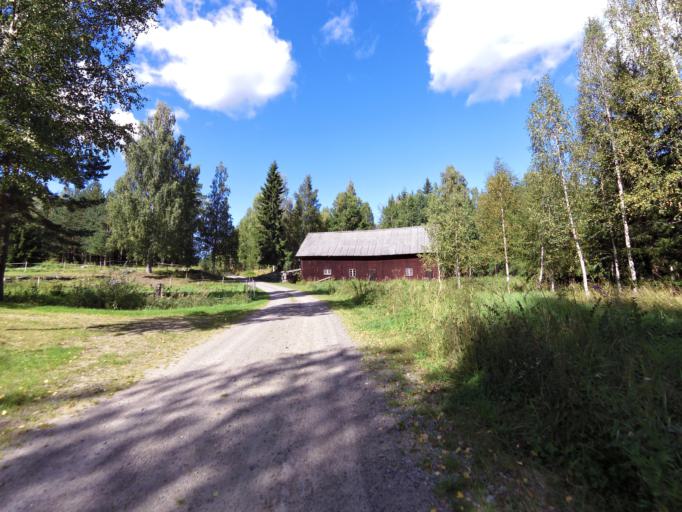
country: SE
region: Gaevleborg
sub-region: Ockelbo Kommun
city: Ockelbo
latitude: 60.8035
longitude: 16.8102
